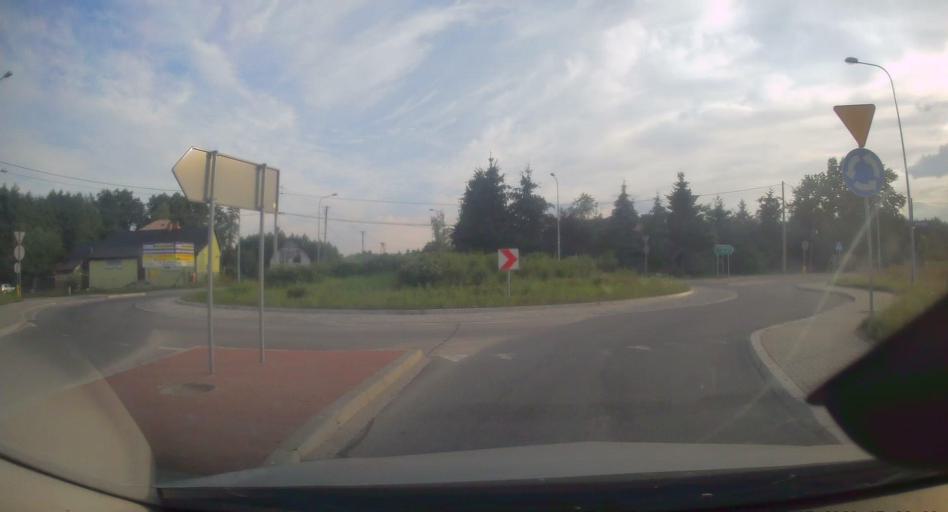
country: PL
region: Lesser Poland Voivodeship
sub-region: Powiat brzeski
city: Przyborow
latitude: 50.0234
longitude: 20.6328
